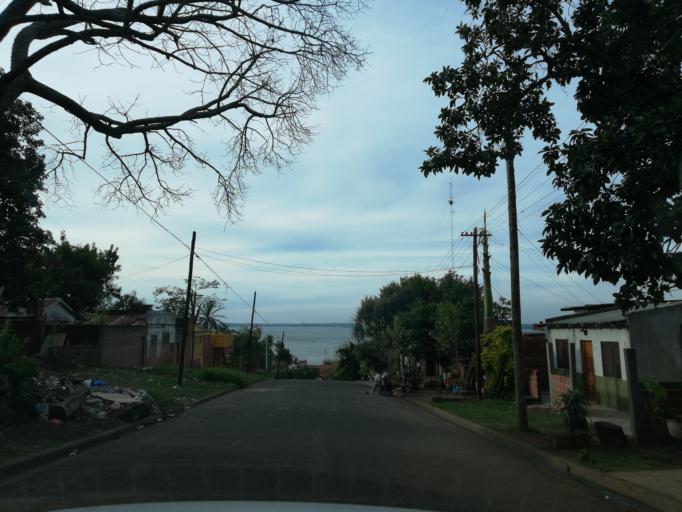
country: AR
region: Misiones
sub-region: Departamento de Capital
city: Posadas
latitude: -27.3559
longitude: -55.9188
